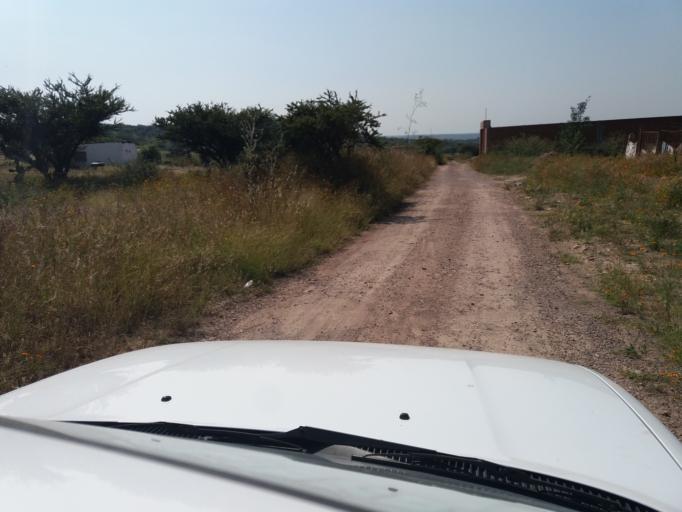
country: MX
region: Aguascalientes
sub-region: Aguascalientes
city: Penuelas (El Cienegal)
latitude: 21.7493
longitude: -102.2520
